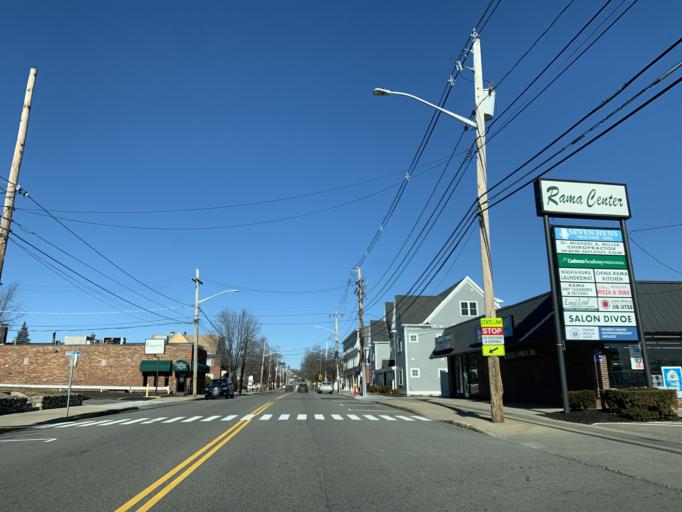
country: US
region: Massachusetts
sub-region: Norfolk County
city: Norwood
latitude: 42.1864
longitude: -71.2030
